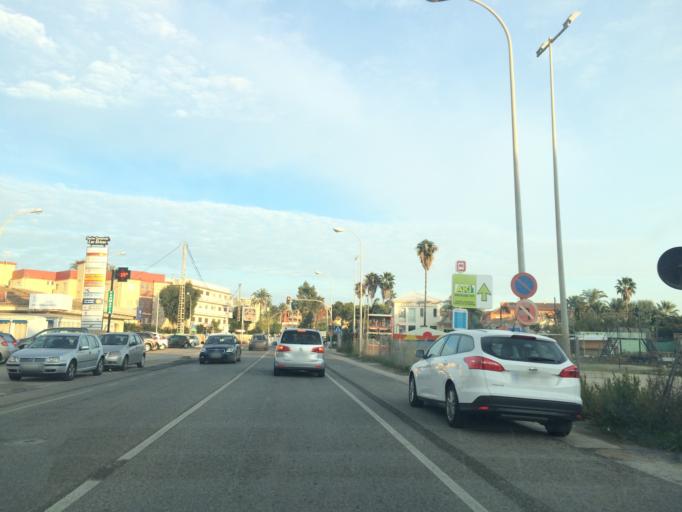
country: ES
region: Valencia
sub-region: Provincia de Alicante
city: Denia
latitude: 38.8561
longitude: 0.0730
